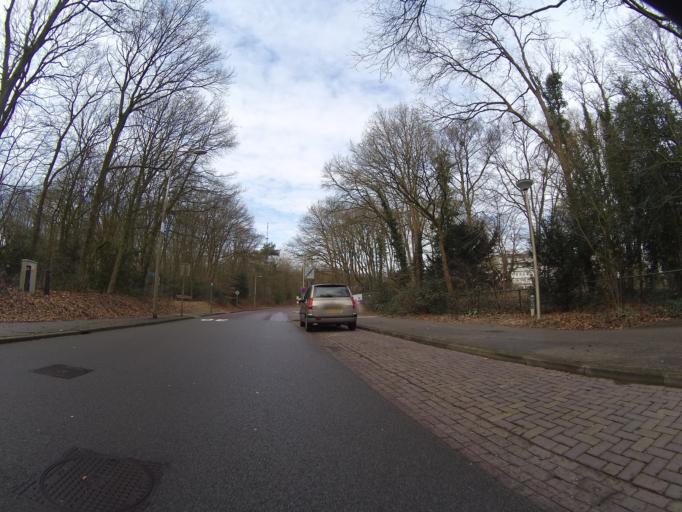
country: NL
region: Utrecht
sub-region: Gemeente Amersfoort
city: Amersfoort
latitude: 52.1423
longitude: 5.3702
